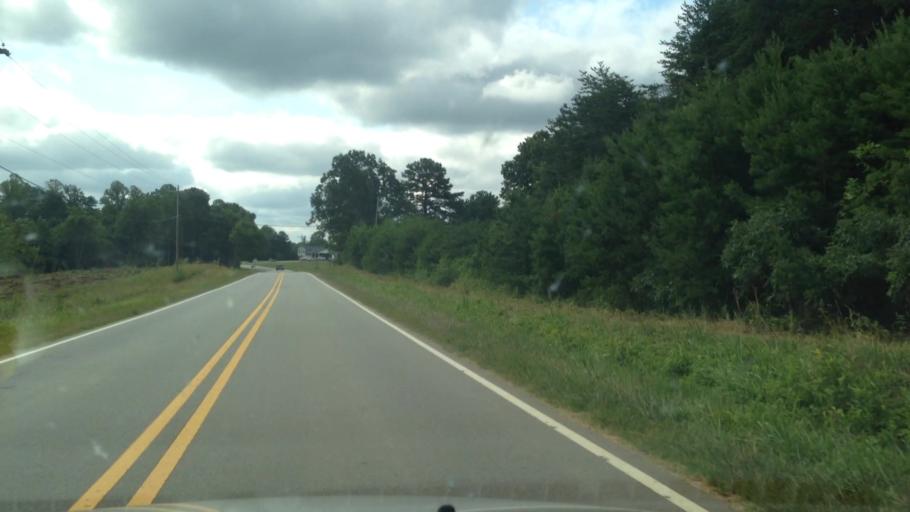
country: US
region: North Carolina
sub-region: Rockingham County
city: Mayodan
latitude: 36.3949
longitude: -80.0163
